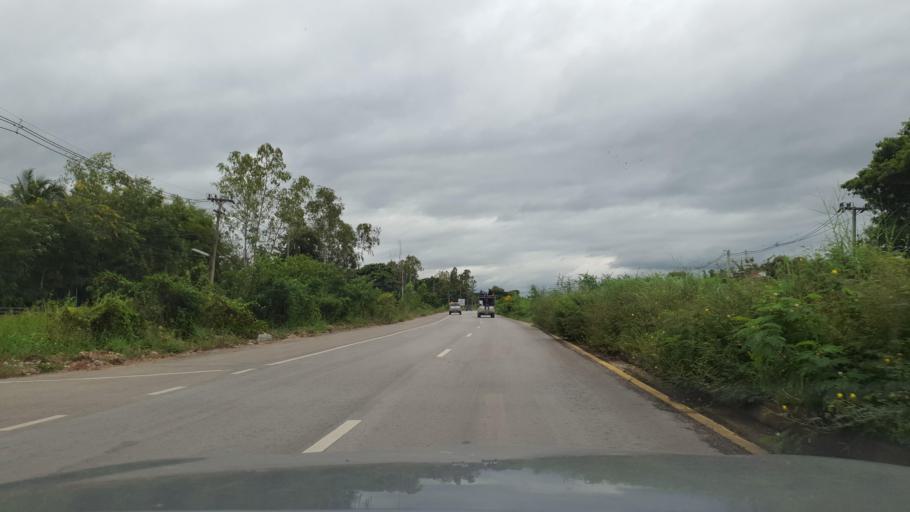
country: TH
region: Lamphun
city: Lamphun
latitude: 18.5878
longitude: 98.9958
